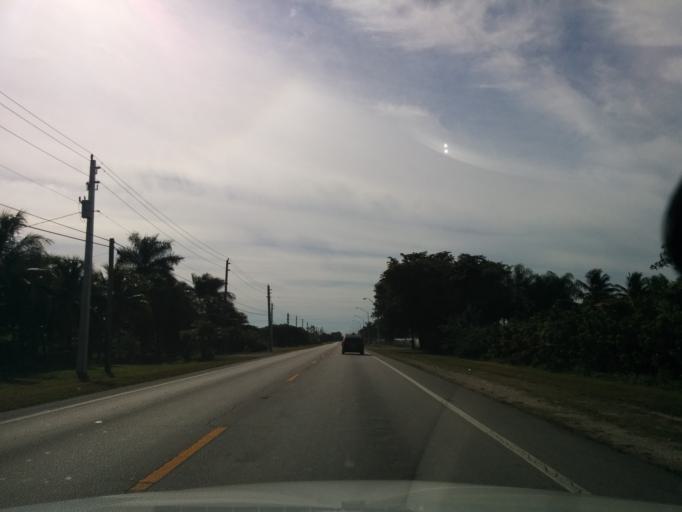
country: US
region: Florida
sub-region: Miami-Dade County
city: Homestead
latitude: 25.5184
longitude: -80.4779
